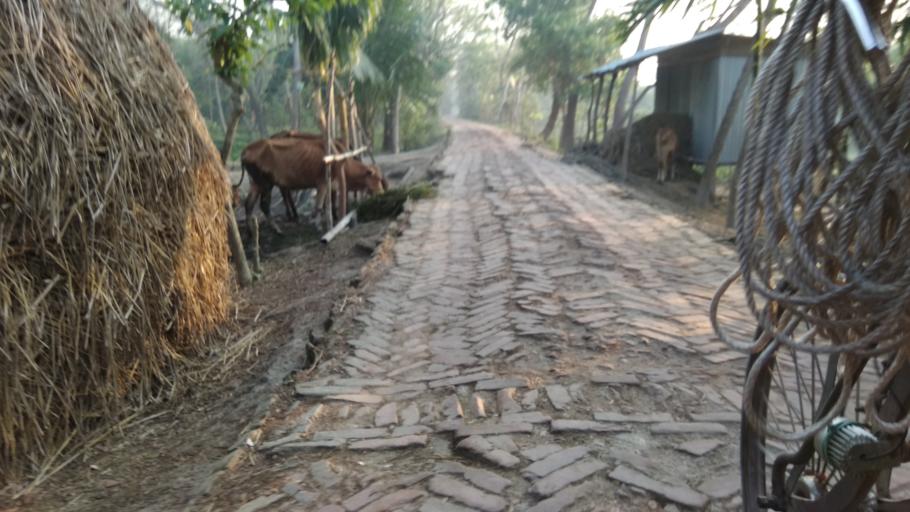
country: BD
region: Barisal
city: Mehendiganj
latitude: 22.9270
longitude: 90.4061
